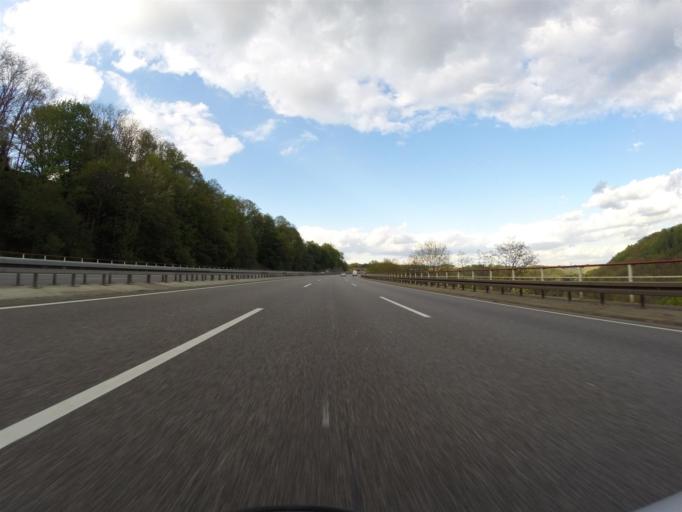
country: DE
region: Saarland
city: Kleinblittersdorf
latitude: 49.2129
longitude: 7.0642
